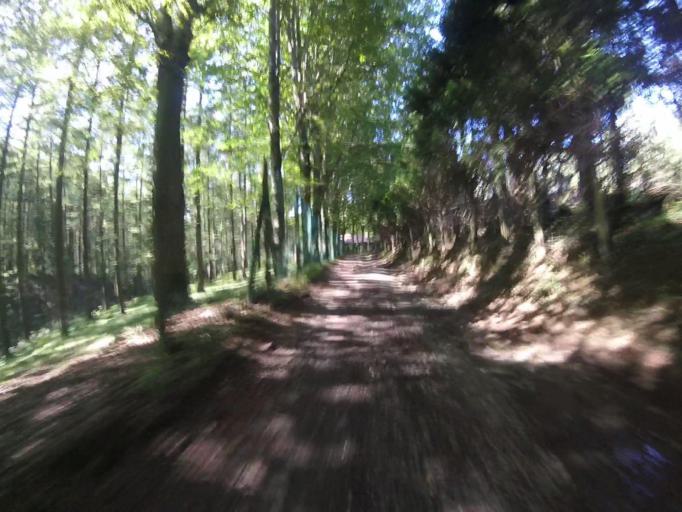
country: ES
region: Basque Country
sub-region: Provincia de Guipuzcoa
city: Irun
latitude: 43.2970
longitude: -1.7998
